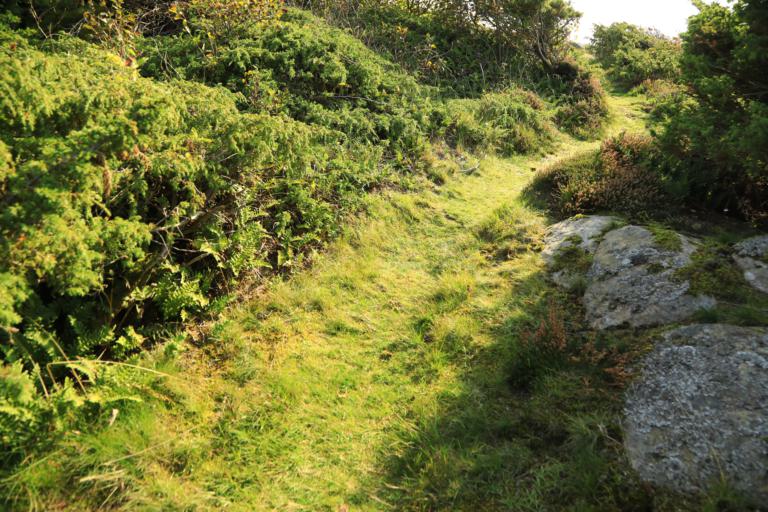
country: SE
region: Halland
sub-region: Varbergs Kommun
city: Varberg
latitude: 57.1154
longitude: 12.2101
